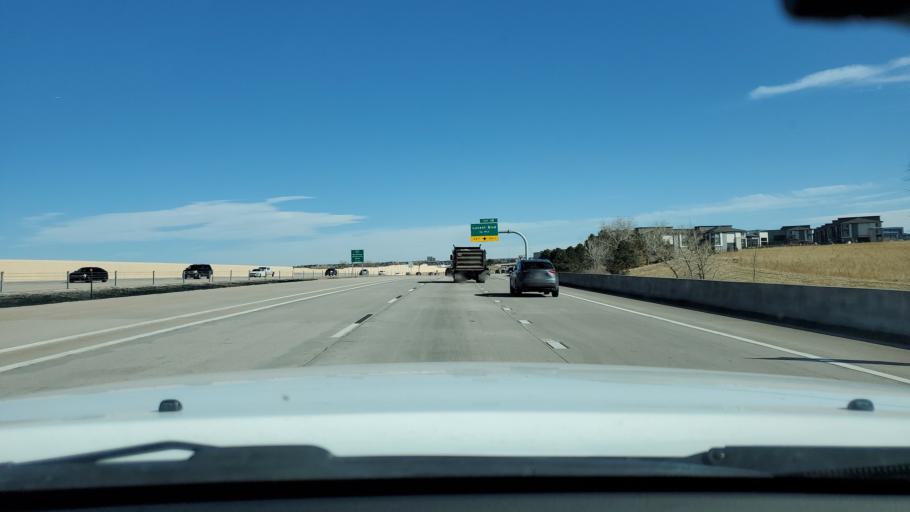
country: US
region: Colorado
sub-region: Arapahoe County
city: Columbine Valley
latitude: 39.5626
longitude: -105.0213
